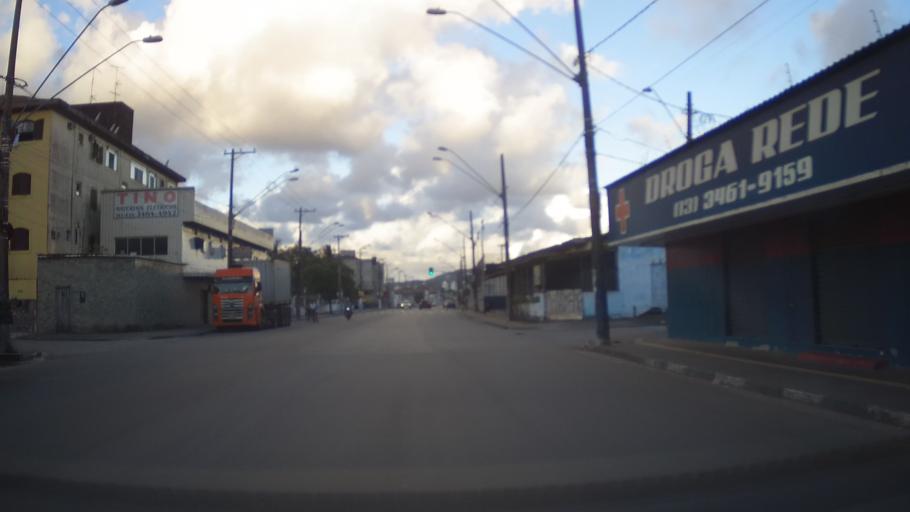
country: BR
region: Sao Paulo
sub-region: Sao Vicente
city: Sao Vicente
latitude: -23.9507
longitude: -46.4048
